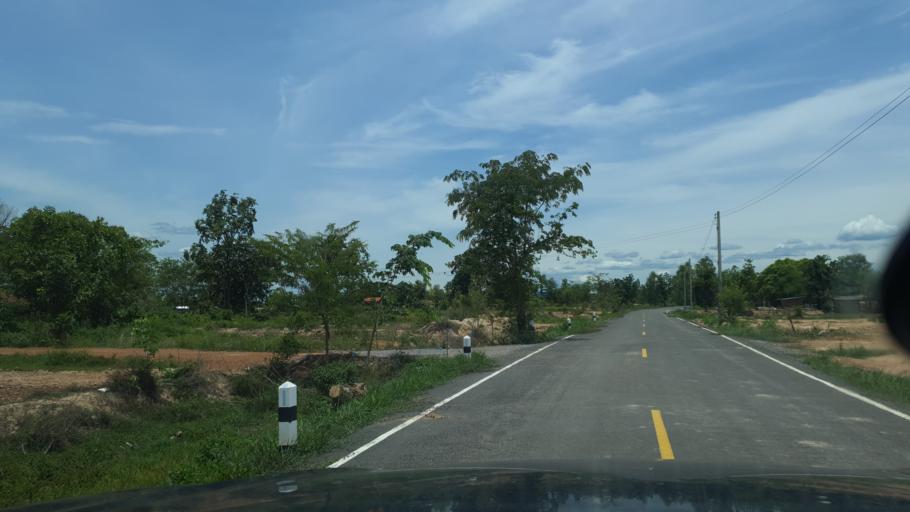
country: TH
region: Sukhothai
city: Ban Na
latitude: 17.1502
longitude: 99.6594
